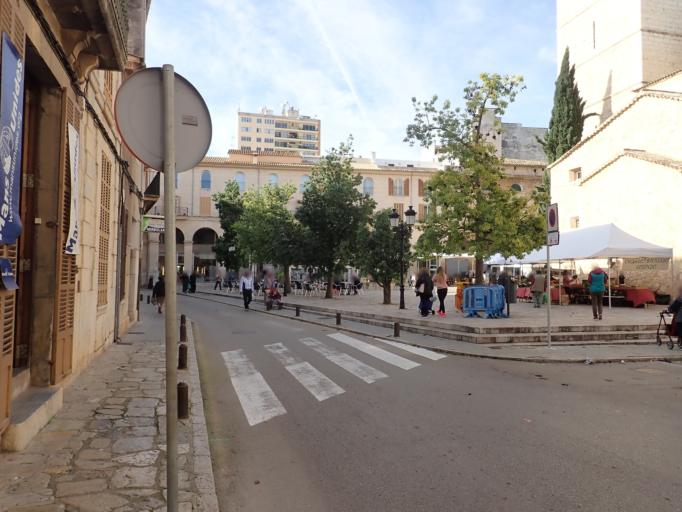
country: ES
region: Balearic Islands
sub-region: Illes Balears
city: Inca
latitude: 39.7213
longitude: 2.9121
